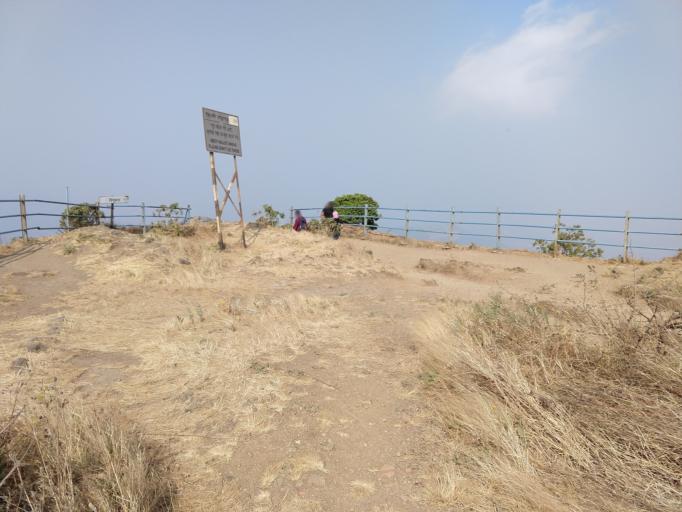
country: IN
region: Maharashtra
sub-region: Pune Division
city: Lonavla
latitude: 18.7114
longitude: 73.4741
